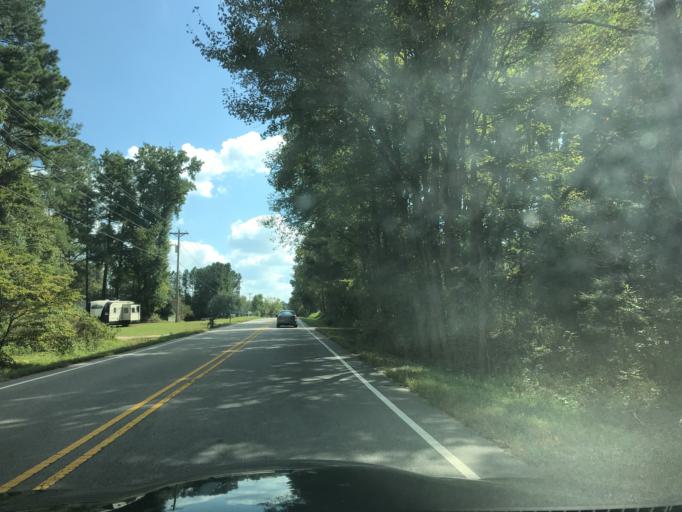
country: US
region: North Carolina
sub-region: Wake County
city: Rolesville
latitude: 35.9016
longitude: -78.5247
